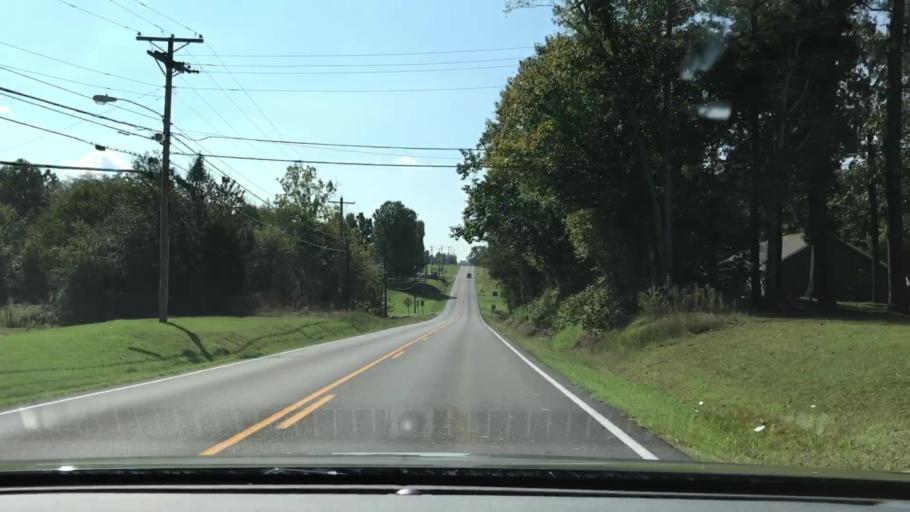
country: US
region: Kentucky
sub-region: Marshall County
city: Benton
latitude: 36.8342
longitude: -88.3506
